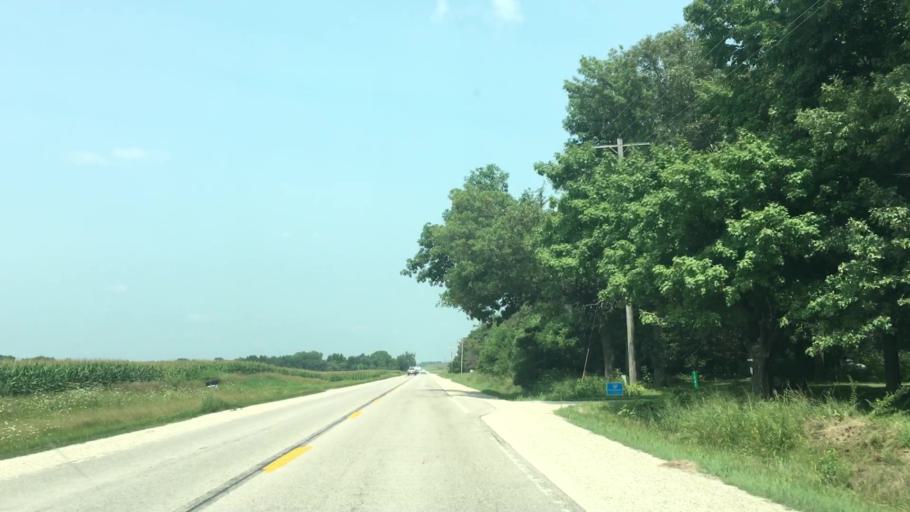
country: US
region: Iowa
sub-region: Buchanan County
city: Independence
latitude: 42.3495
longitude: -91.8893
